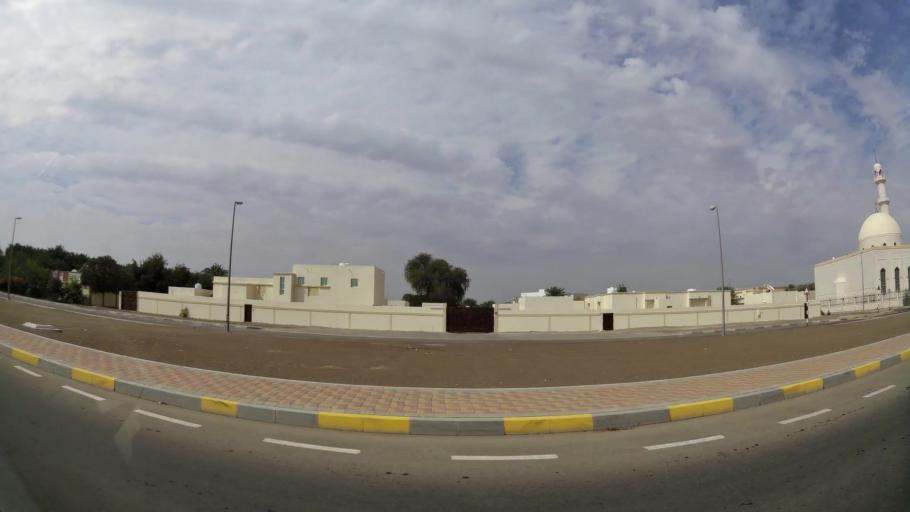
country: AE
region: Abu Dhabi
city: Al Ain
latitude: 24.1905
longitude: 55.8016
